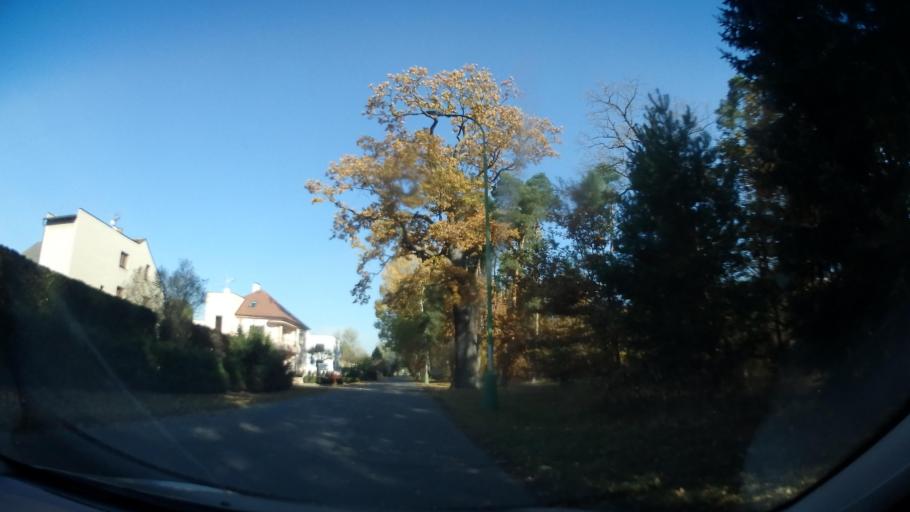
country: CZ
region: Kralovehradecky
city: Trebechovice pod Orebem
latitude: 50.1972
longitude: 16.0036
